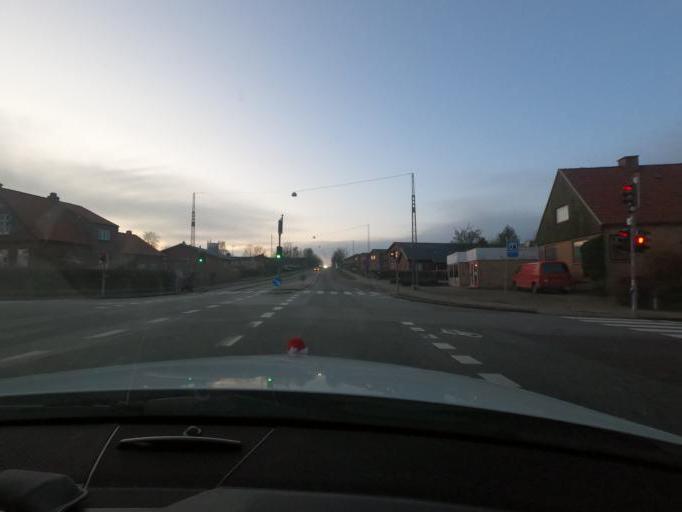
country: DK
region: South Denmark
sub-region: Sonderborg Kommune
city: Sonderborg
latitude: 54.9188
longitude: 9.7939
